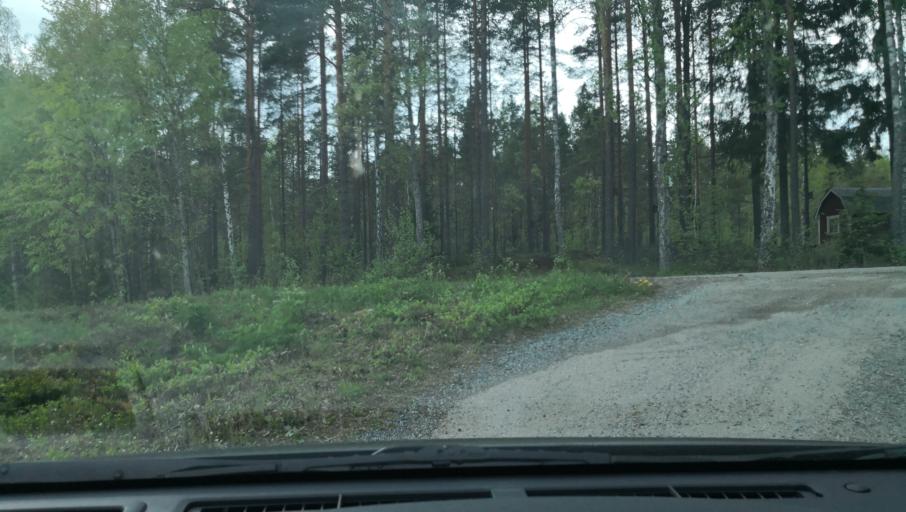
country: SE
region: Vaestmanland
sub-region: Skinnskattebergs Kommun
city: Skinnskatteberg
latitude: 59.8317
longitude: 15.5636
